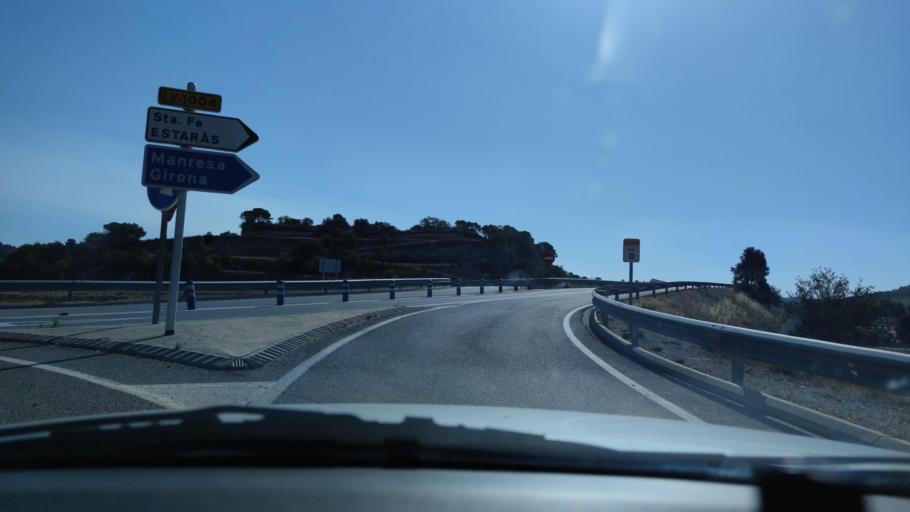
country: ES
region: Catalonia
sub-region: Provincia de Lleida
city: Cervera
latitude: 41.6958
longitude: 1.3456
